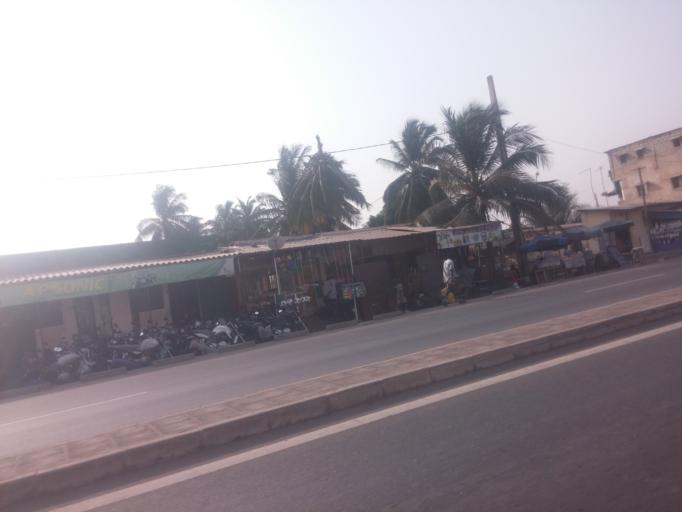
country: TG
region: Maritime
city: Lome
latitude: 6.1696
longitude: 1.2825
